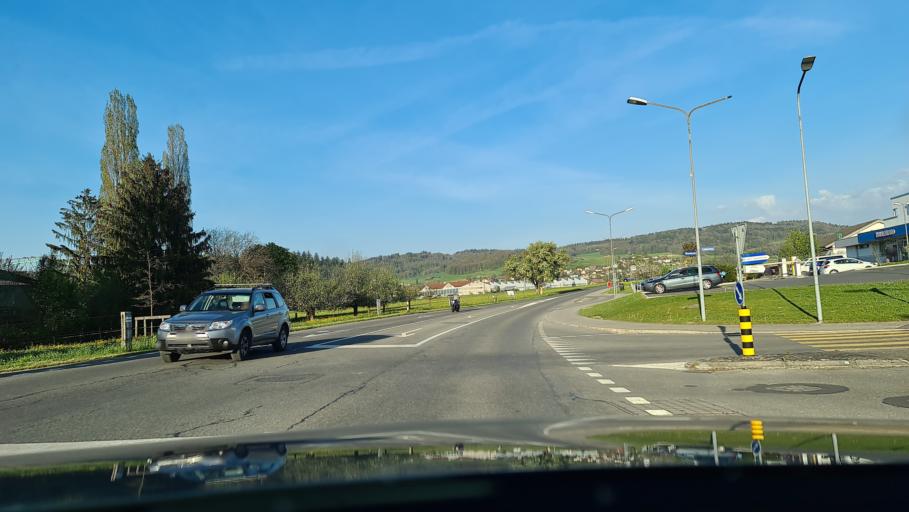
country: CH
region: Aargau
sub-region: Bezirk Lenzburg
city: Seon
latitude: 47.3473
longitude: 8.1667
